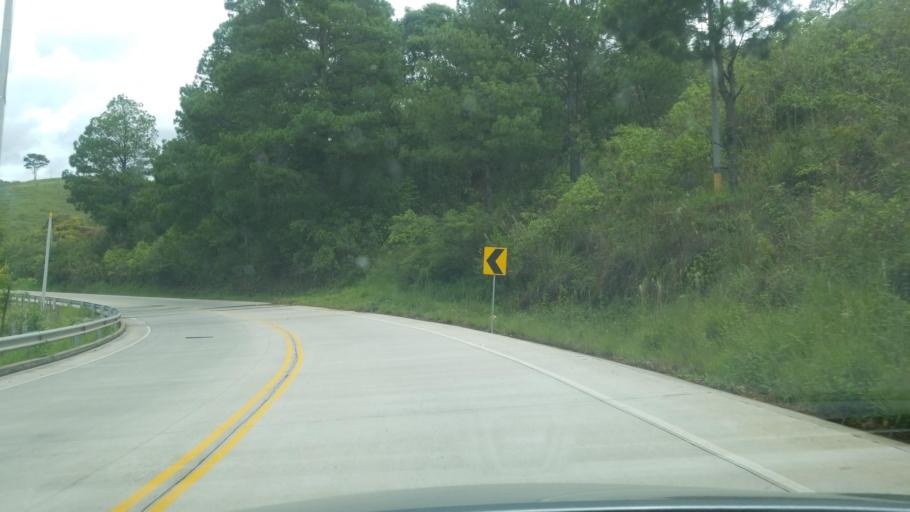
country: HN
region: Copan
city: San Jeronimo
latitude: 14.9337
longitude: -88.9326
